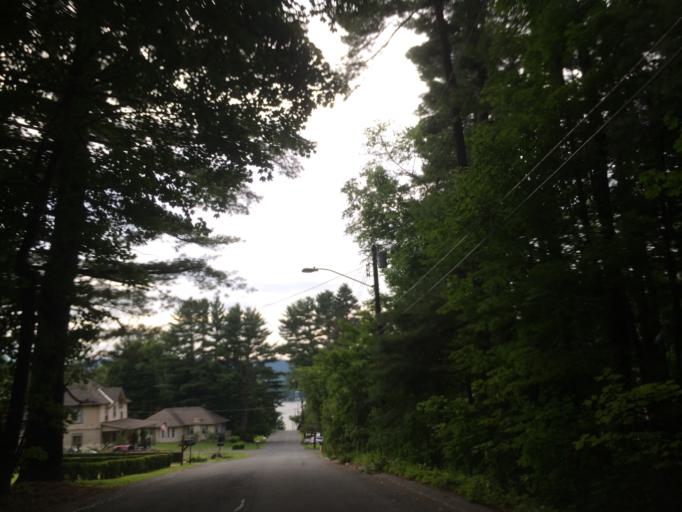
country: US
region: Massachusetts
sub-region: Berkshire County
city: Lanesborough
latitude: 42.4903
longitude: -73.2387
